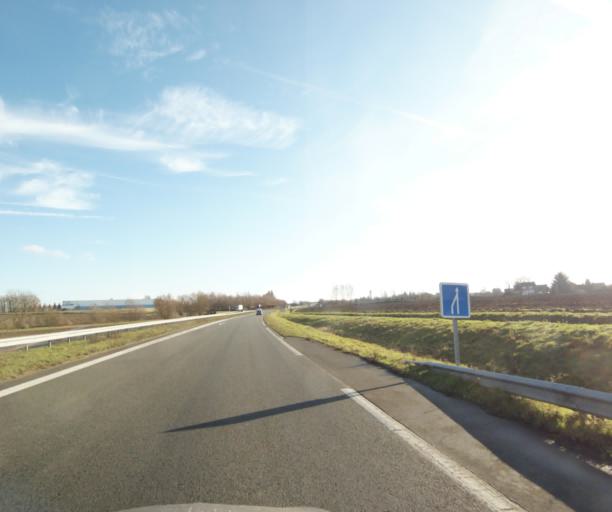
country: FR
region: Nord-Pas-de-Calais
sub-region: Departement du Nord
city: Saultain
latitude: 50.3437
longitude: 3.5813
